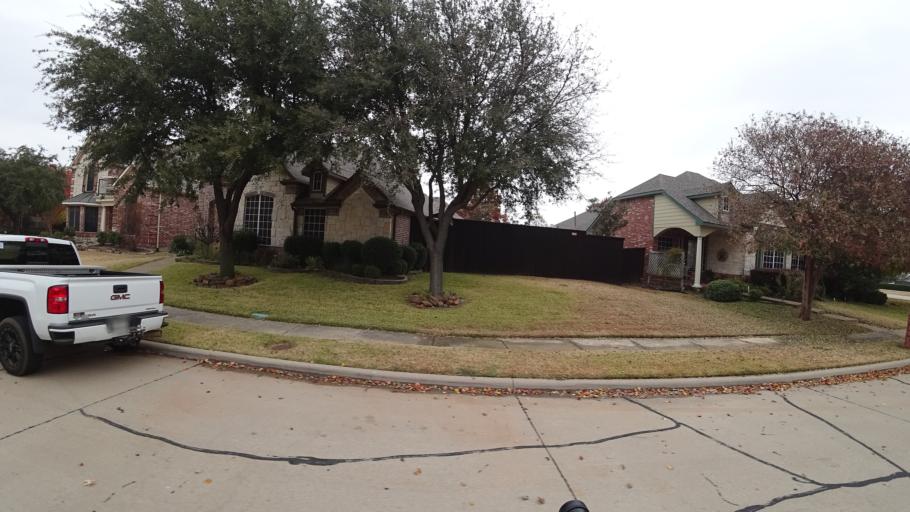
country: US
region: Texas
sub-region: Denton County
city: Lewisville
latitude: 33.0273
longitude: -96.9349
